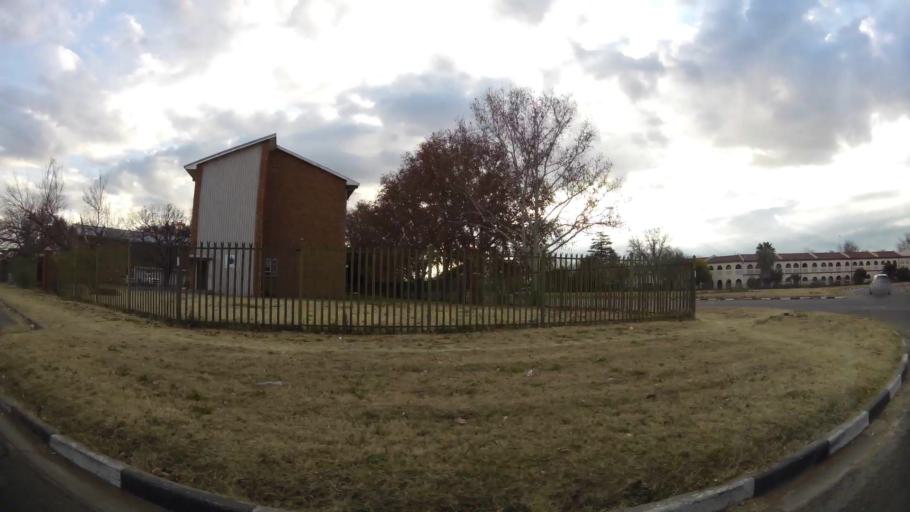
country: ZA
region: Orange Free State
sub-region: Lejweleputswa District Municipality
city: Welkom
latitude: -27.9873
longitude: 26.7118
